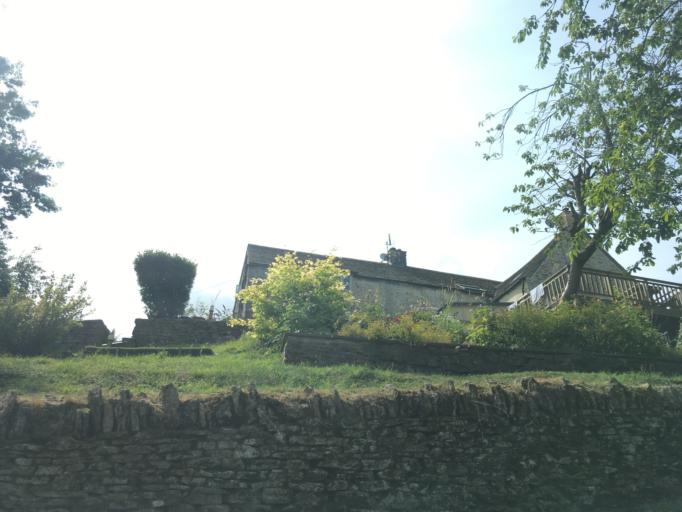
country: GB
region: England
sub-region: Gloucestershire
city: Nailsworth
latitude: 51.6768
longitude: -2.2325
